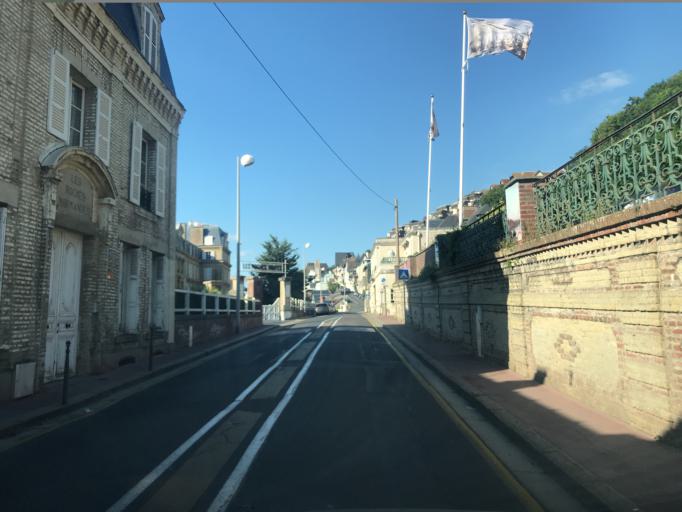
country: FR
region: Lower Normandy
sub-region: Departement du Calvados
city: Trouville-sur-Mer
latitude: 49.3712
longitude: 0.0836
